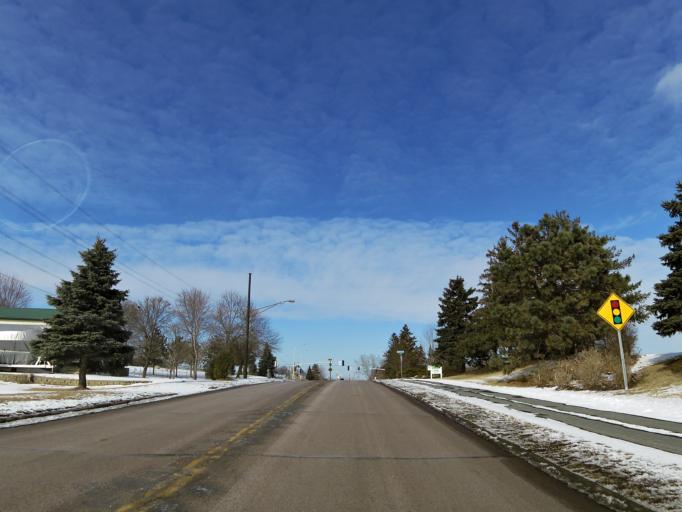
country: US
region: Minnesota
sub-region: Hennepin County
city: Eden Prairie
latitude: 44.8281
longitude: -93.4291
